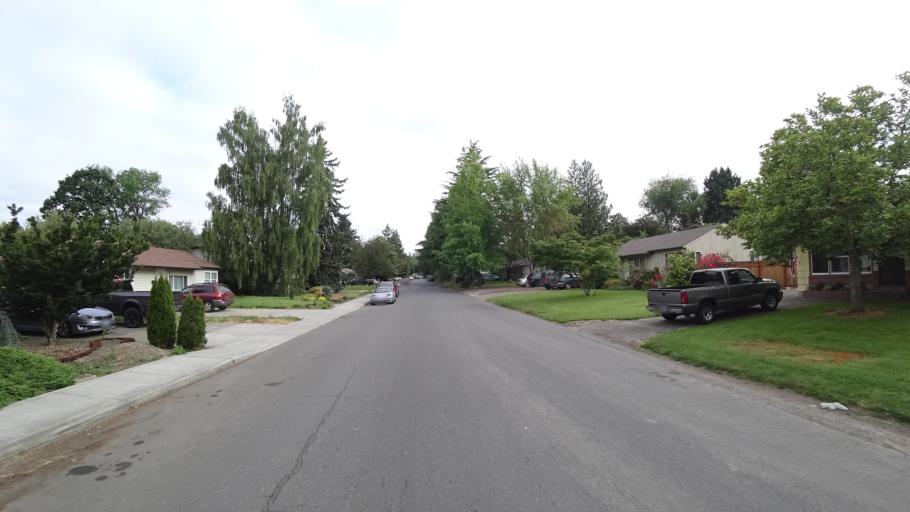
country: US
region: Oregon
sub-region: Washington County
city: Beaverton
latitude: 45.4940
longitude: -122.8044
